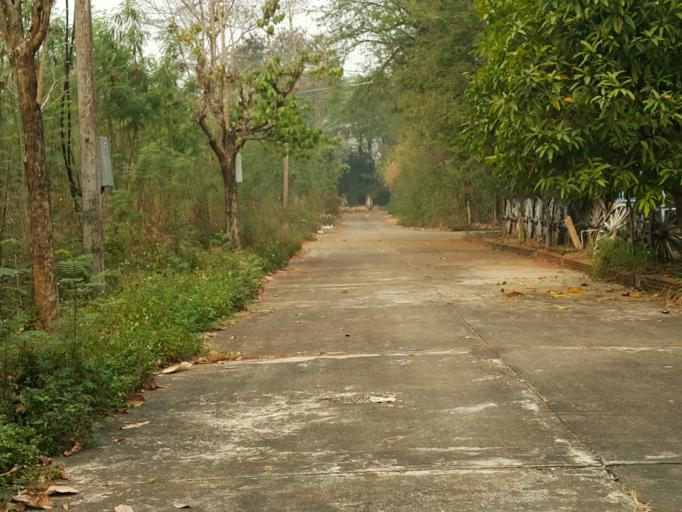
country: TH
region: Chiang Mai
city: San Kamphaeng
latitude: 18.7569
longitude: 99.0910
